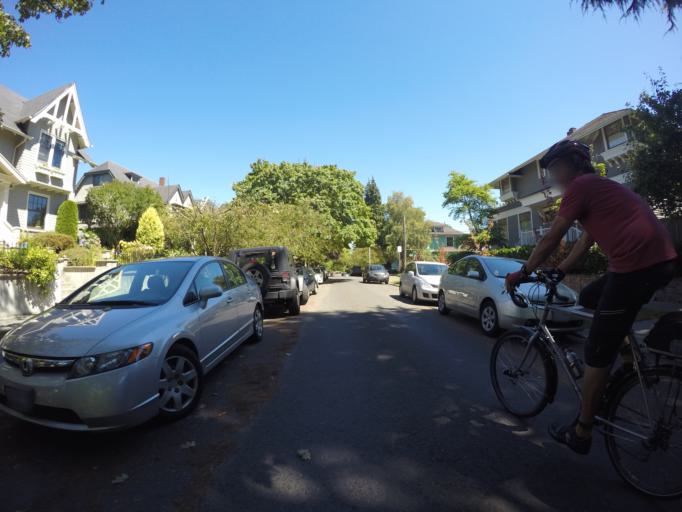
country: US
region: Washington
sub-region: King County
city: Seattle
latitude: 47.6253
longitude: -122.3140
